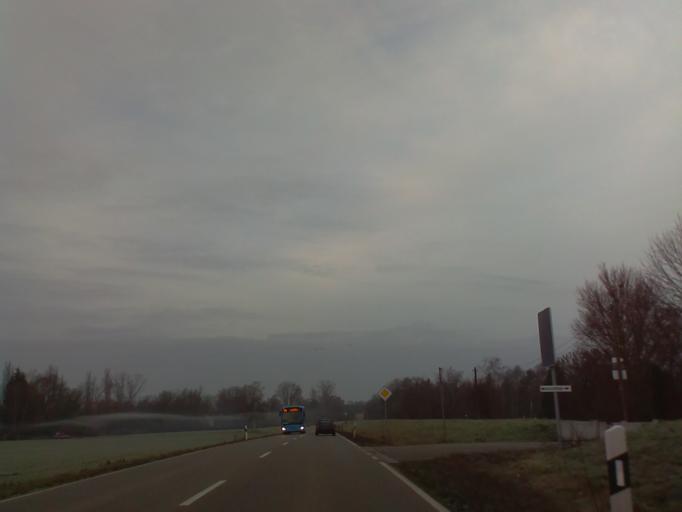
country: DE
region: Rheinland-Pfalz
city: Altrip
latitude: 49.4379
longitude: 8.4618
